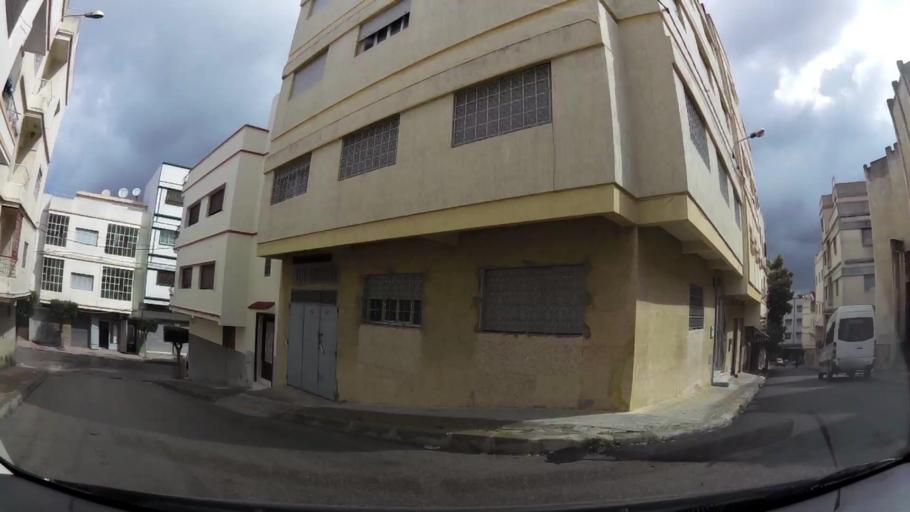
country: MA
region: Tanger-Tetouan
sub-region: Tanger-Assilah
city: Tangier
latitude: 35.7563
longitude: -5.8200
